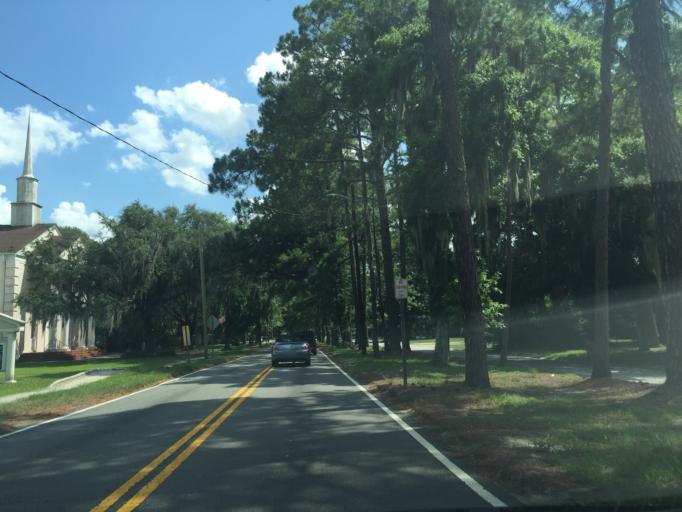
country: US
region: Georgia
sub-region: Chatham County
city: Savannah
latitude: 32.0356
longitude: -81.1086
